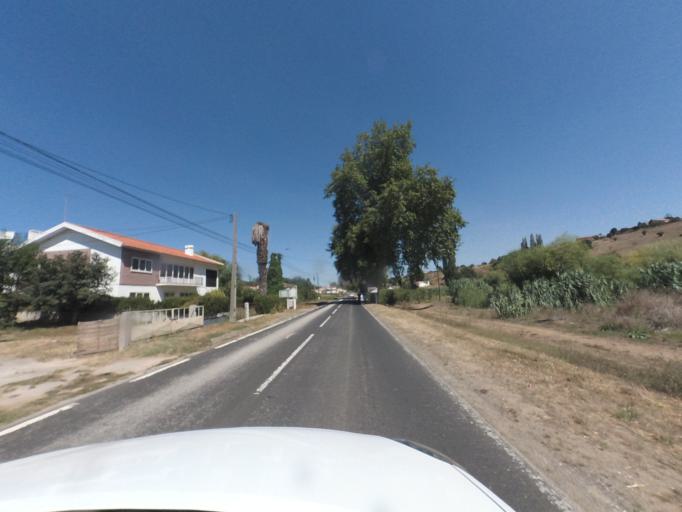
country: PT
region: Leiria
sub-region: Alcobaca
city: Alcobaca
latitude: 39.5231
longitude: -9.0043
